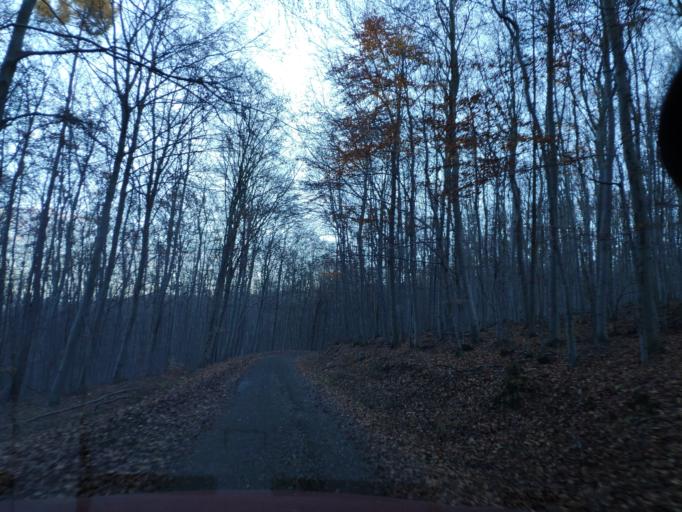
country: SK
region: Kosicky
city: Secovce
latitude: 48.5836
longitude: 21.5015
